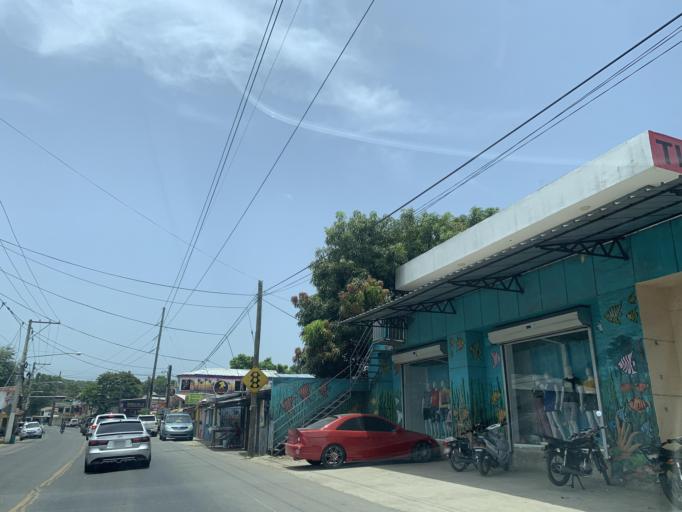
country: DO
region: Puerto Plata
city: Cabarete
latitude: 19.7444
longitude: -70.5231
